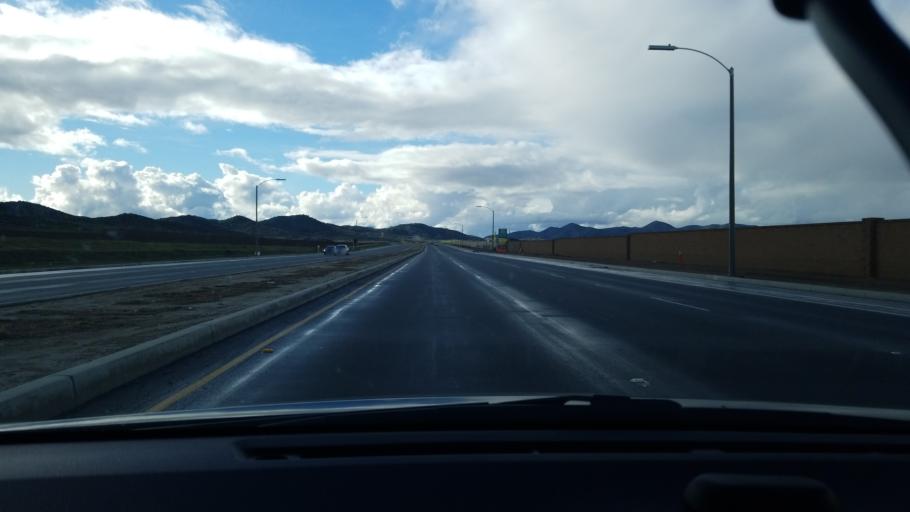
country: US
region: California
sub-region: Riverside County
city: Winchester
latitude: 33.6926
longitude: -117.1003
